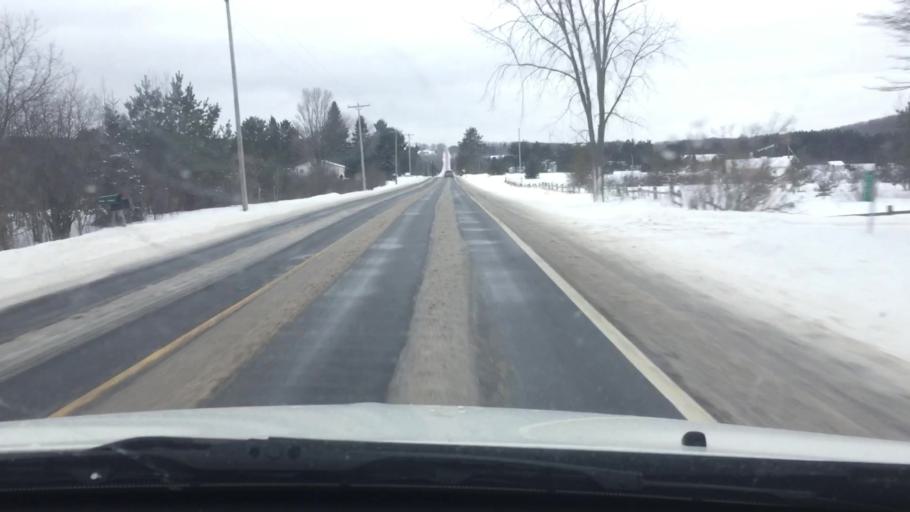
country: US
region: Michigan
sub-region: Charlevoix County
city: East Jordan
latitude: 45.1326
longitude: -85.1312
